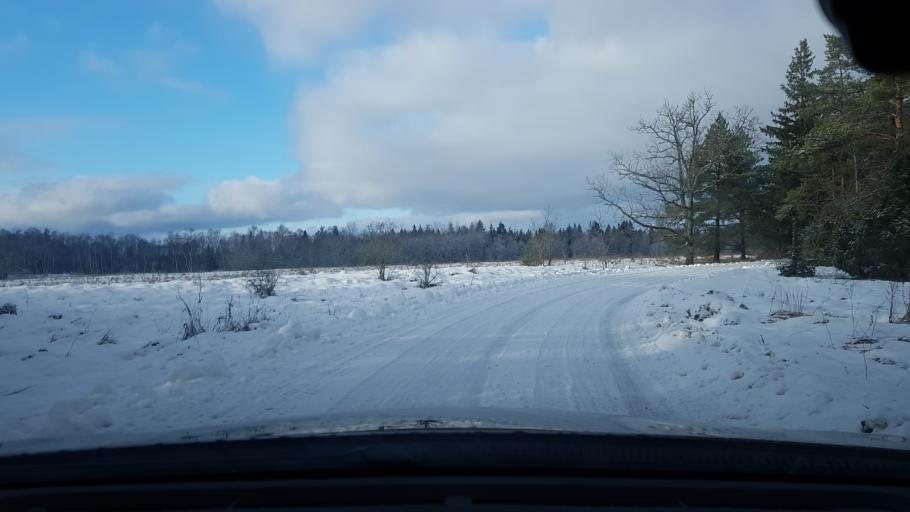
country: EE
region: Harju
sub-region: Keila linn
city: Keila
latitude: 59.2820
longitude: 24.2613
